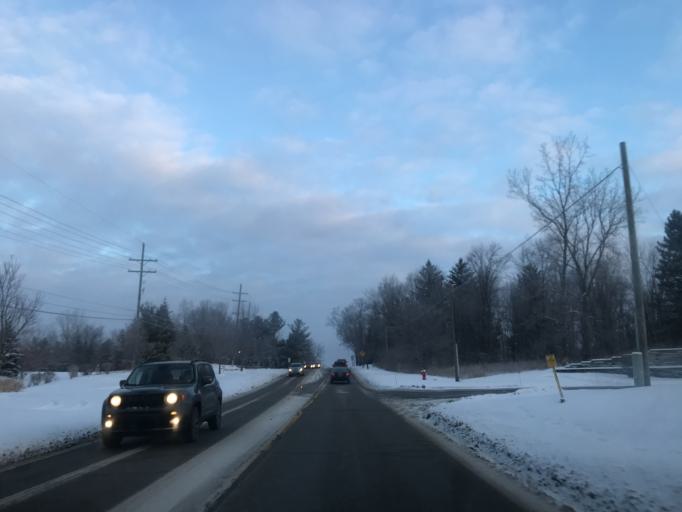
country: US
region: Michigan
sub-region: Oakland County
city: Wixom
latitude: 42.4845
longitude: -83.5351
